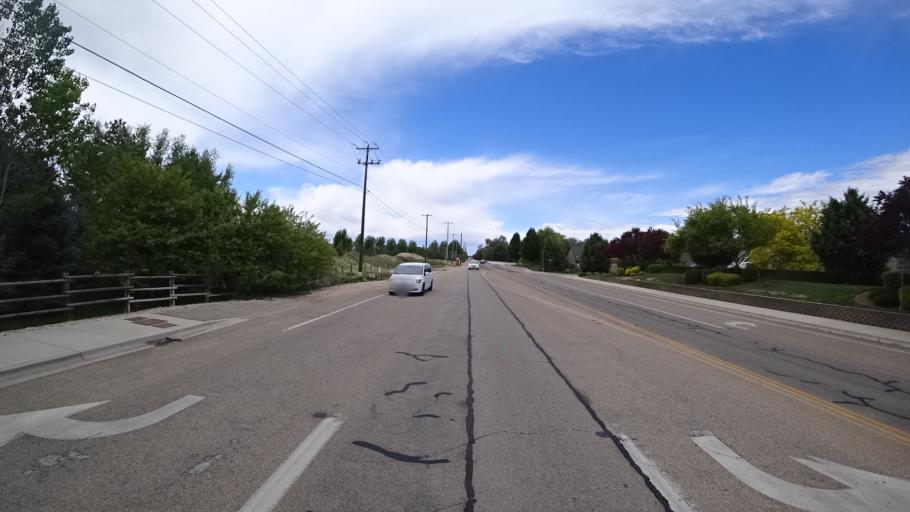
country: US
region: Idaho
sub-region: Ada County
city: Meridian
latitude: 43.5757
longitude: -116.3355
